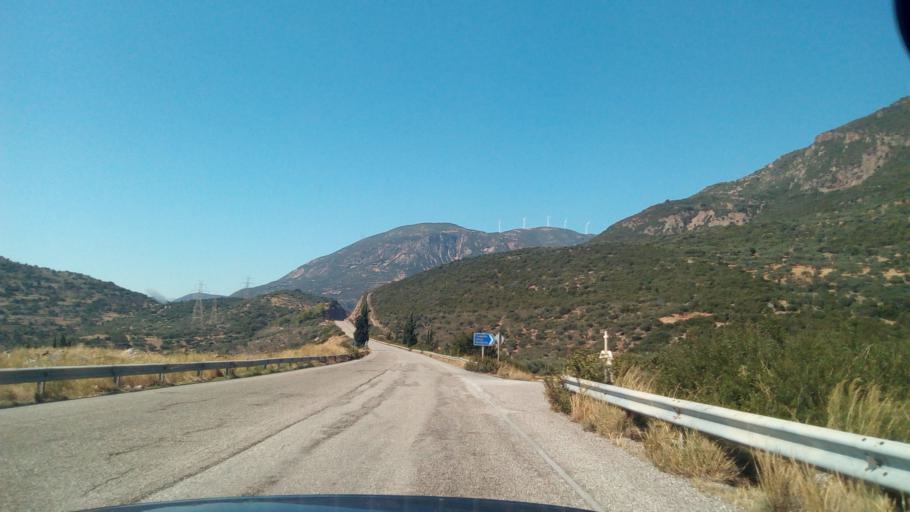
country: GR
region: West Greece
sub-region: Nomos Achaias
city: Selianitika
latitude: 38.3845
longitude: 22.0876
